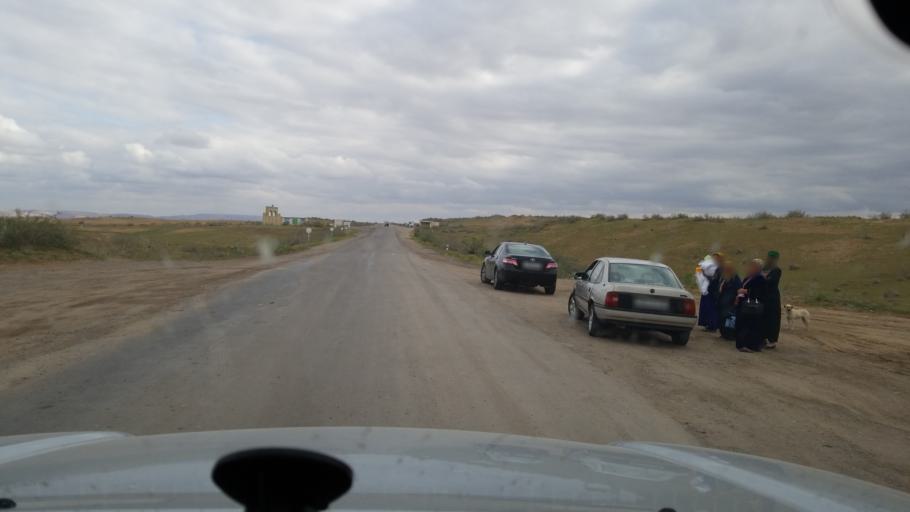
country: TM
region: Mary
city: Serhetabat
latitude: 35.9886
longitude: 62.6268
